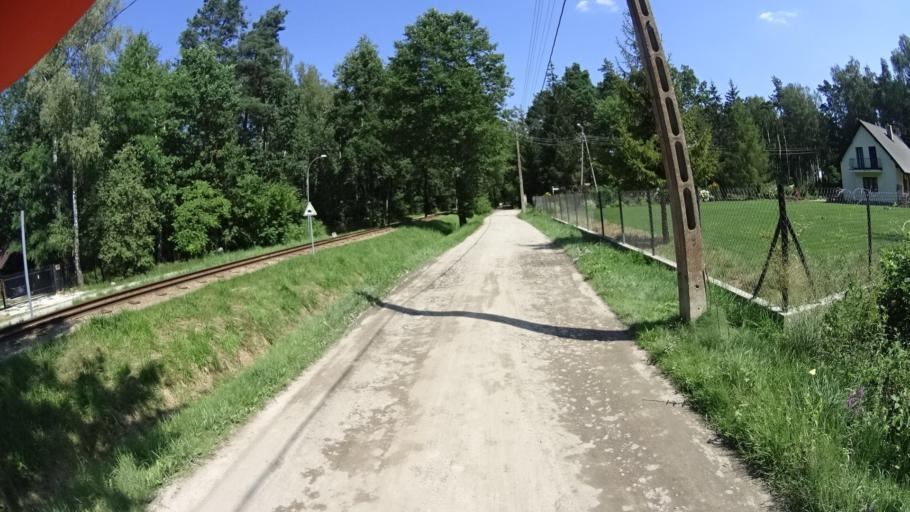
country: PL
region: Masovian Voivodeship
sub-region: Powiat piaseczynski
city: Prazmow
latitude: 52.0077
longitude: 20.9163
